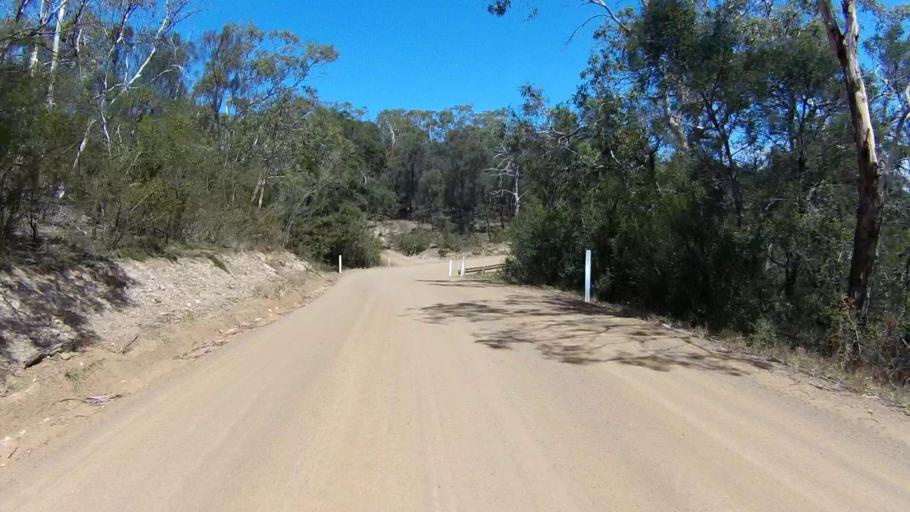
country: AU
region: Tasmania
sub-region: Clarence
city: Lauderdale
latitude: -42.9347
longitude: 147.4632
